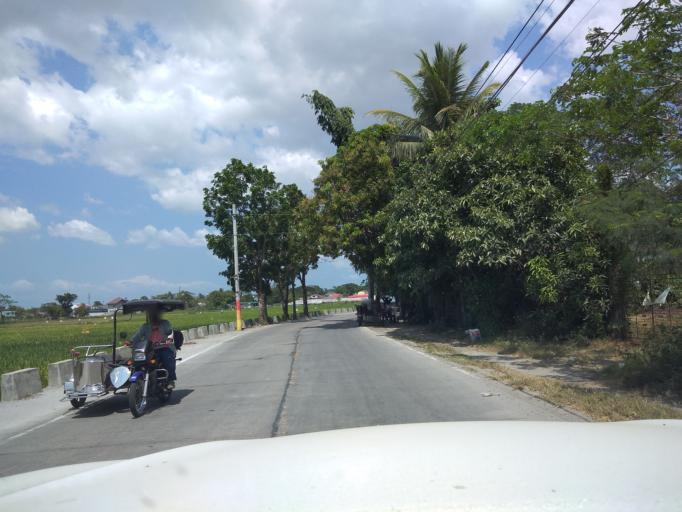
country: PH
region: Central Luzon
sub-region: Province of Pampanga
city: Bahay Pare
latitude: 15.0178
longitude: 120.8835
